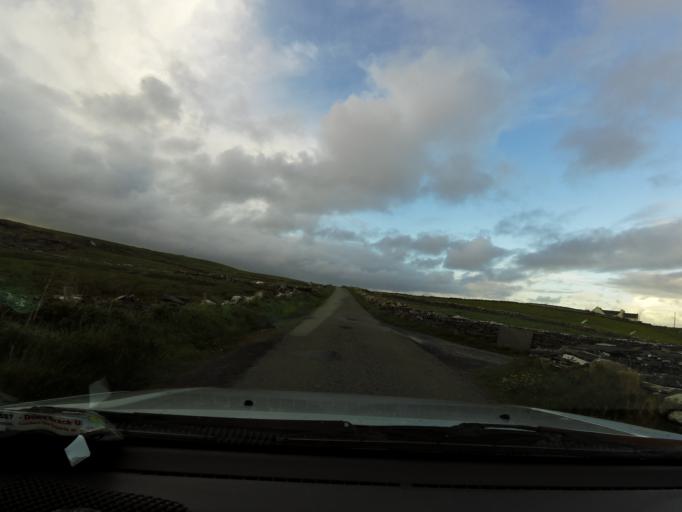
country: IE
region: Munster
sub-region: An Clar
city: Kilrush
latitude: 52.9548
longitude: -9.4378
